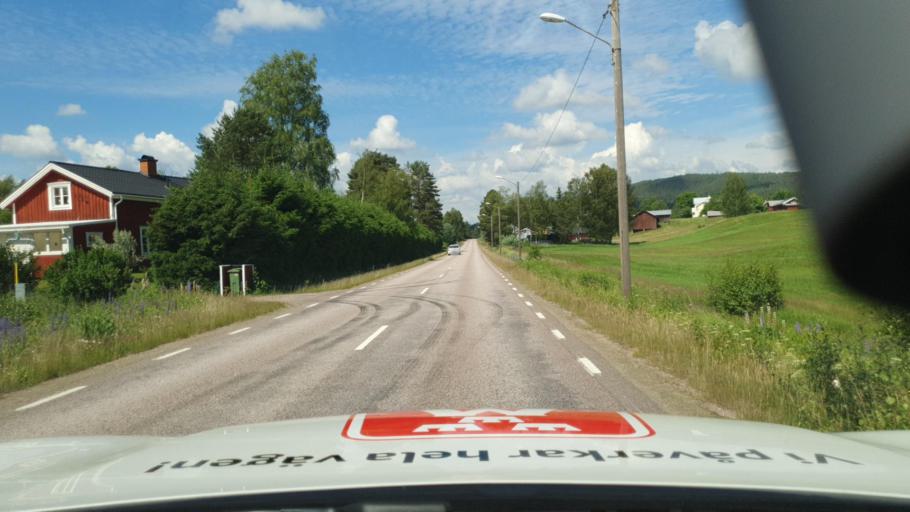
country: SE
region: Vaermland
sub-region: Torsby Kommun
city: Torsby
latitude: 60.3317
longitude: 13.0060
